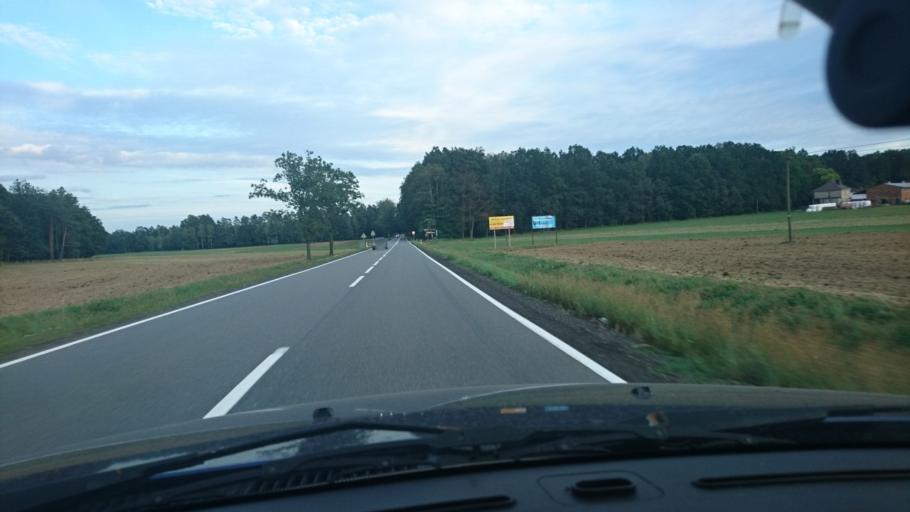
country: PL
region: Opole Voivodeship
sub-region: Powiat oleski
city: Olesno
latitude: 50.8537
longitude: 18.4641
